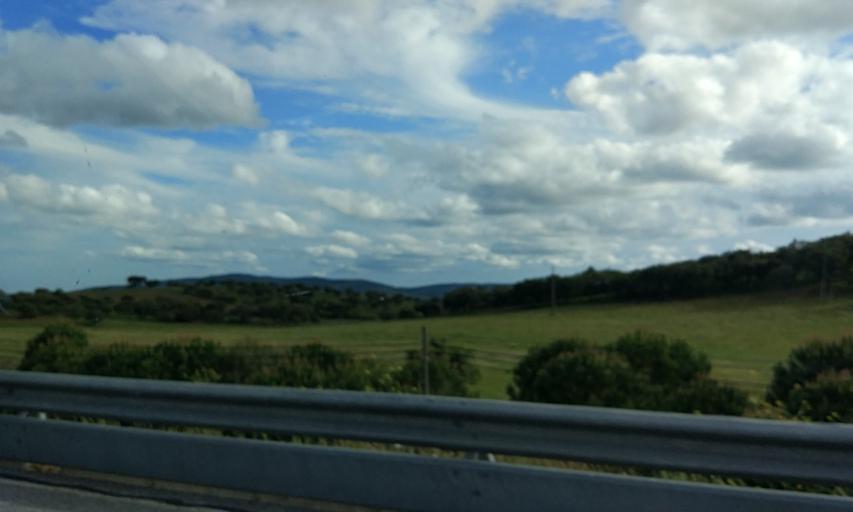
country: PT
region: Evora
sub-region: Estremoz
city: Estremoz
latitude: 38.8143
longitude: -7.5557
